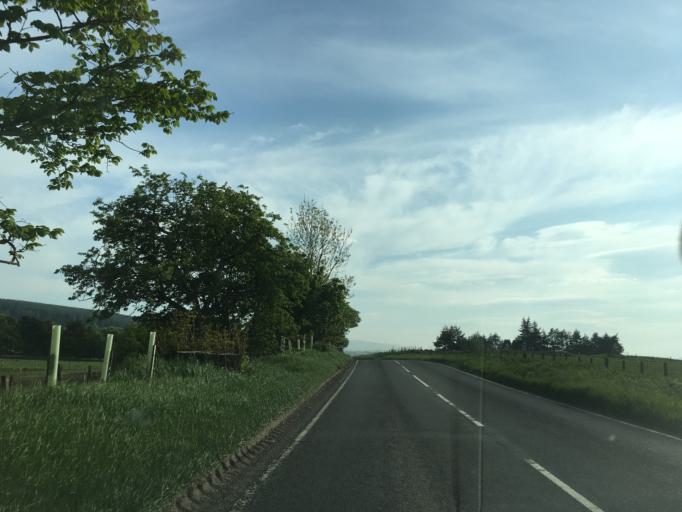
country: GB
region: Scotland
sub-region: The Scottish Borders
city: West Linton
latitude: 55.7454
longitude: -3.2937
